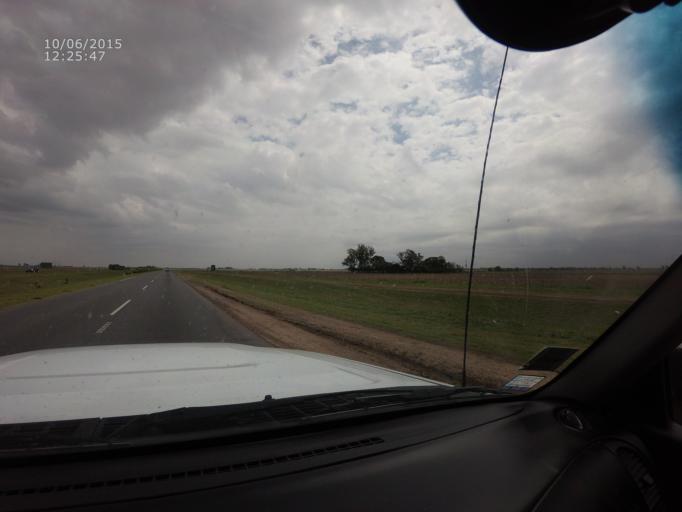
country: AR
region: Santa Fe
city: Roldan
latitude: -32.9055
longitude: -61.0051
